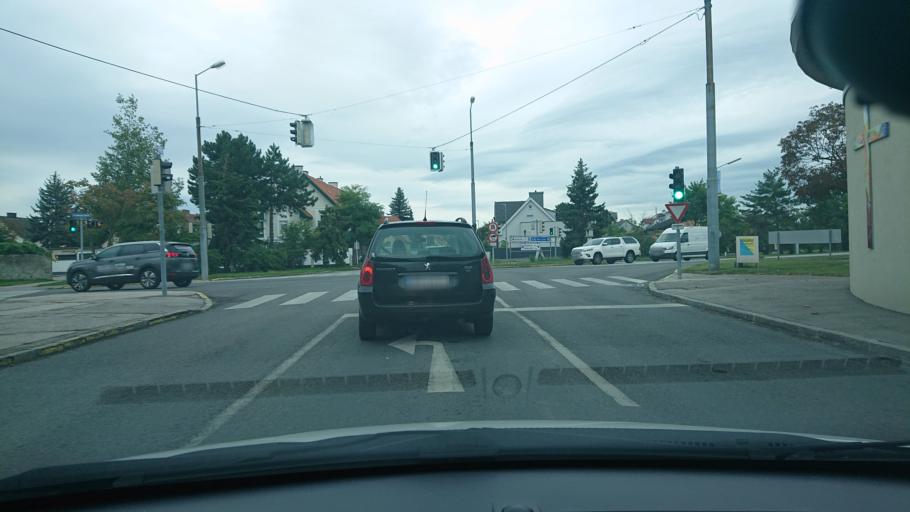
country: AT
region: Lower Austria
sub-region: Wiener Neustadt Stadt
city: Wiener Neustadt
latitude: 47.8080
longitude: 16.2227
